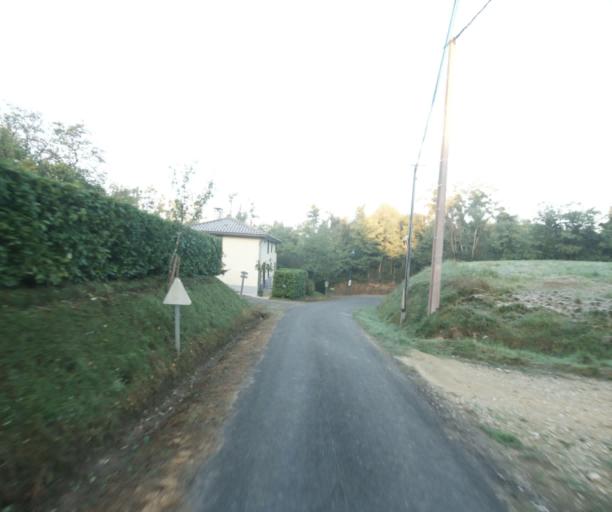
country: FR
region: Midi-Pyrenees
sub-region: Departement du Gers
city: Eauze
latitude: 43.8086
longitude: 0.1655
